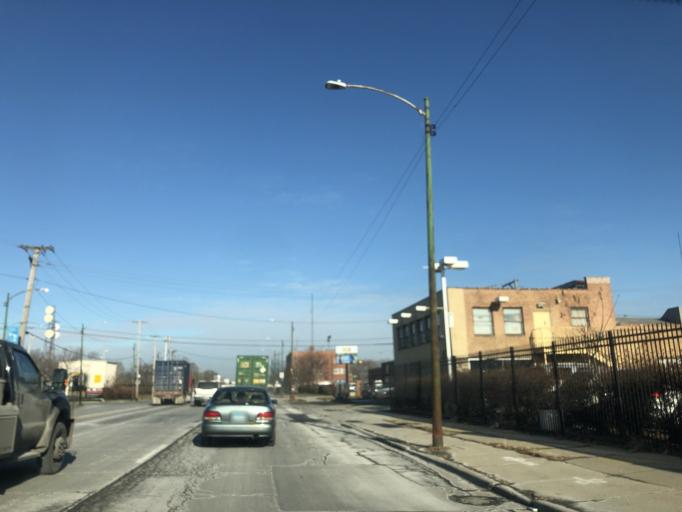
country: US
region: Illinois
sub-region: Cook County
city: Evergreen Park
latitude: 41.7550
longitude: -87.6829
